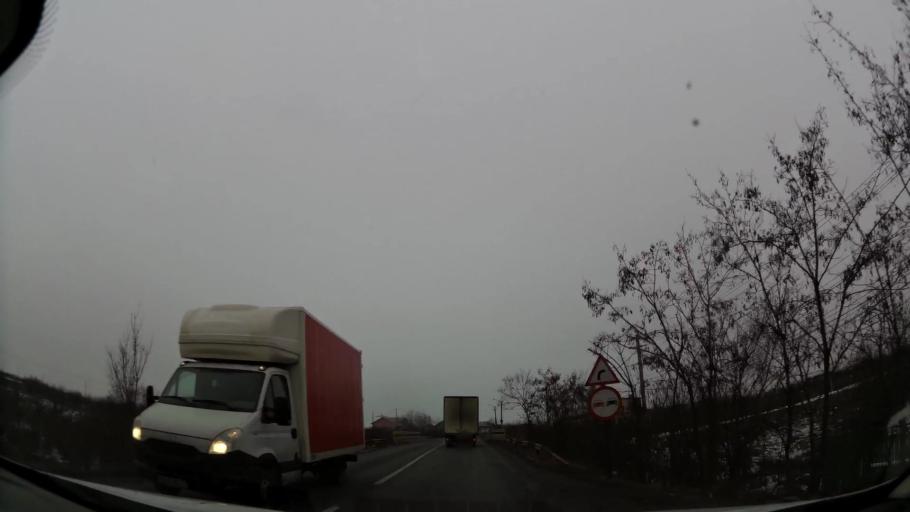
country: RO
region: Dambovita
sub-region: Comuna Racari
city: Mavrodin
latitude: 44.6383
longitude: 25.7130
